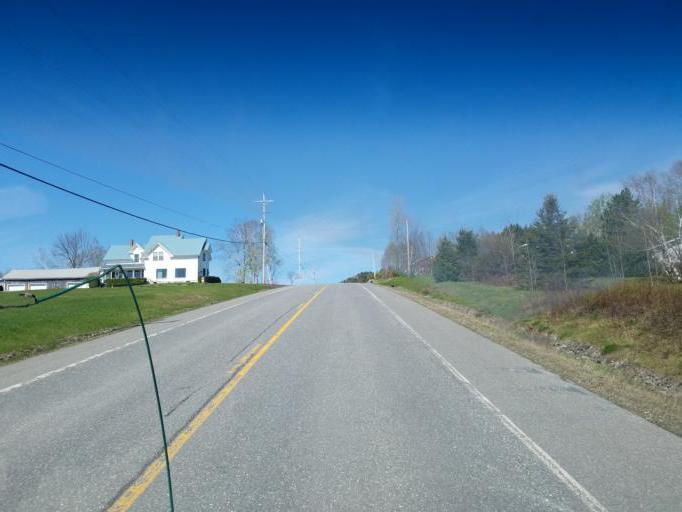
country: US
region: Maine
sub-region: Aroostook County
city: Presque Isle
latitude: 46.6667
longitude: -68.2098
